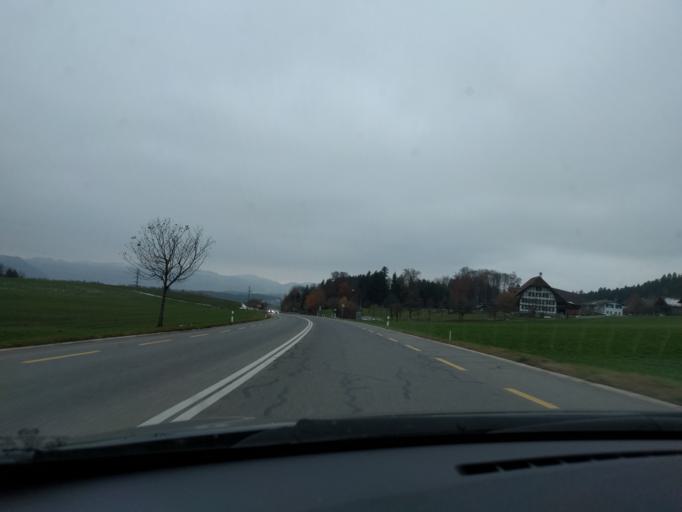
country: CH
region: Bern
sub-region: Bern-Mittelland District
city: Biglen
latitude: 46.9179
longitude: 7.6071
